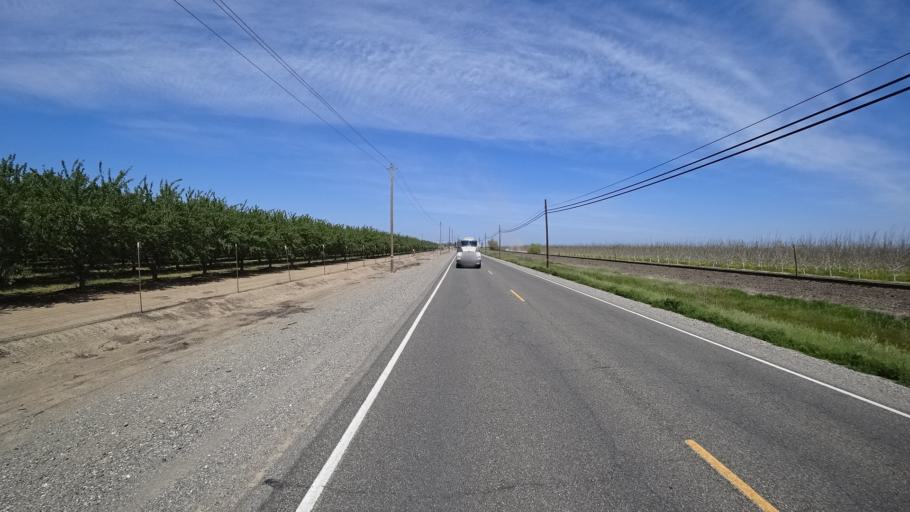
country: US
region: California
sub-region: Glenn County
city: Willows
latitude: 39.6018
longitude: -122.1940
